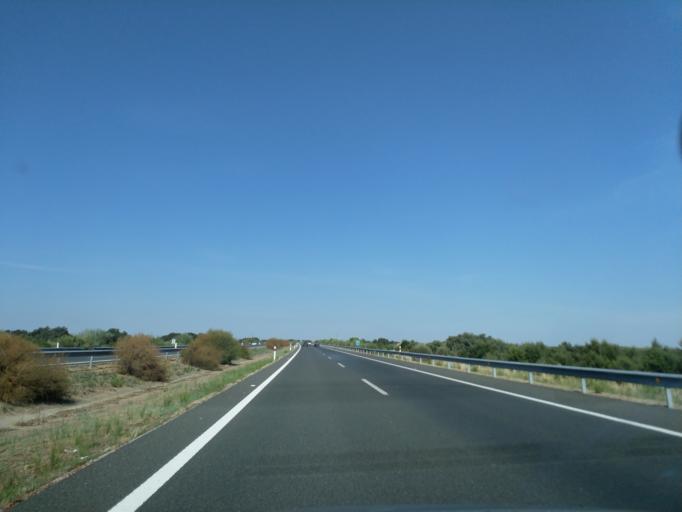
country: ES
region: Extremadura
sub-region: Provincia de Caceres
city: Aldea del Cano
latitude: 39.2599
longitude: -6.3139
